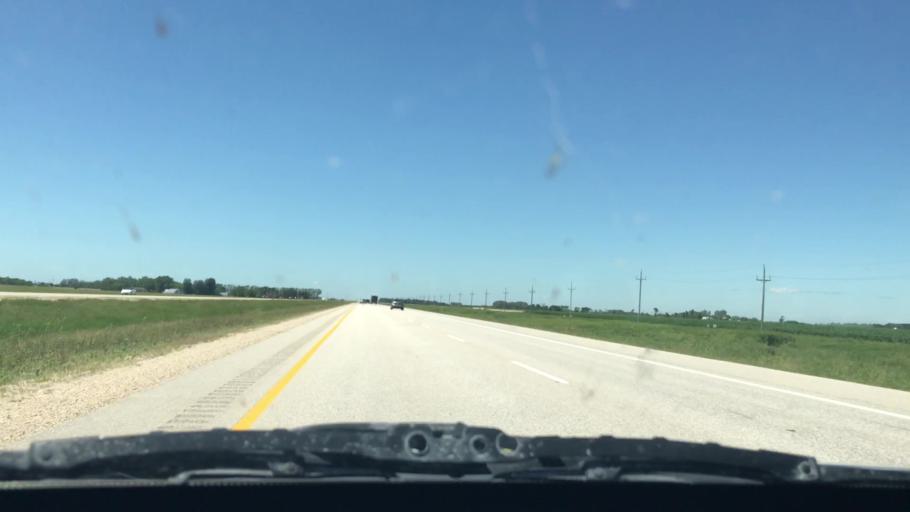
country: CA
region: Manitoba
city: Steinbach
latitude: 49.7269
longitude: -96.7104
